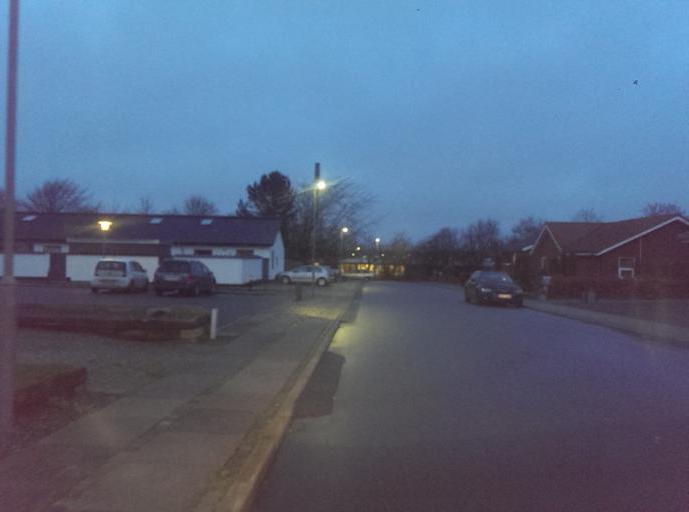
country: DK
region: South Denmark
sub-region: Esbjerg Kommune
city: Tjaereborg
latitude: 55.5010
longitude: 8.5357
